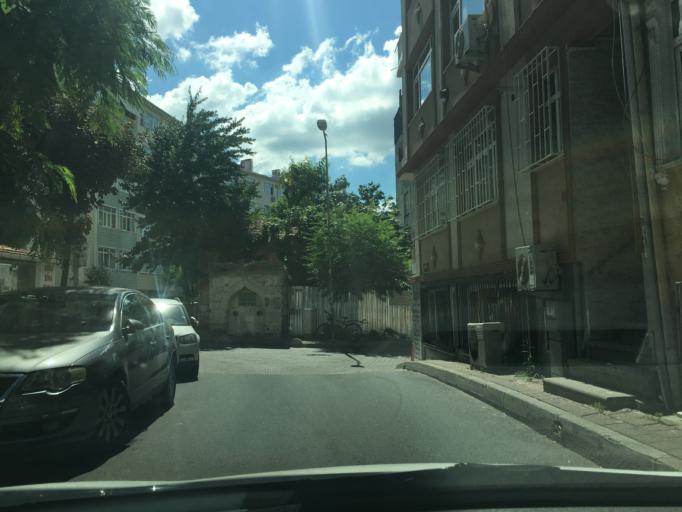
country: TR
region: Istanbul
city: Istanbul
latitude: 41.0090
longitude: 28.9289
